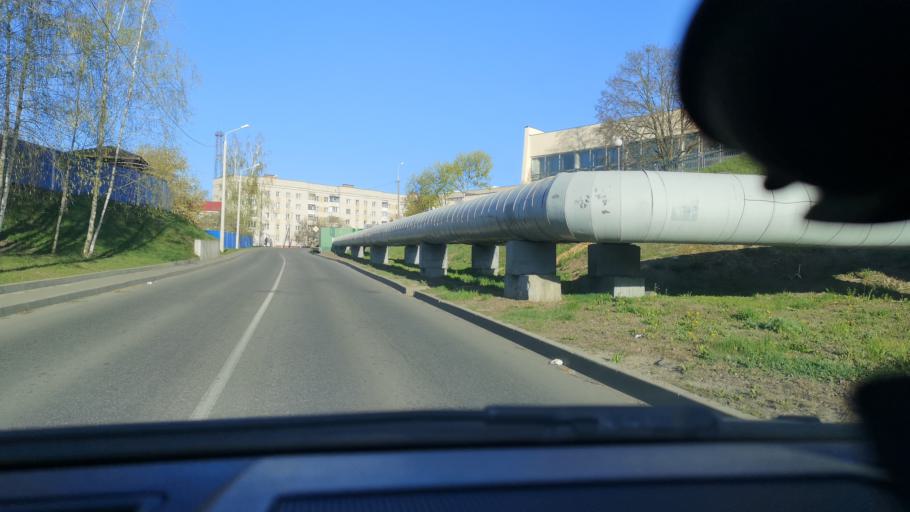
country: BY
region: Gomel
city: Gomel
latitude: 52.4510
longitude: 31.0095
